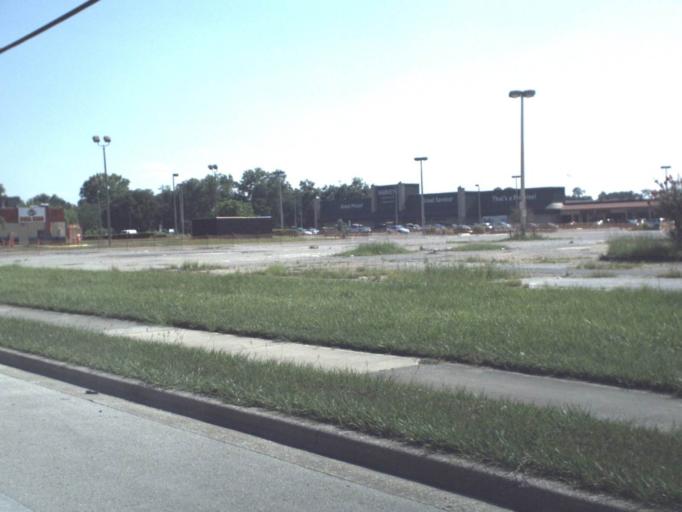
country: US
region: Florida
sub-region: Duval County
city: Jacksonville
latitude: 30.3396
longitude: -81.7312
